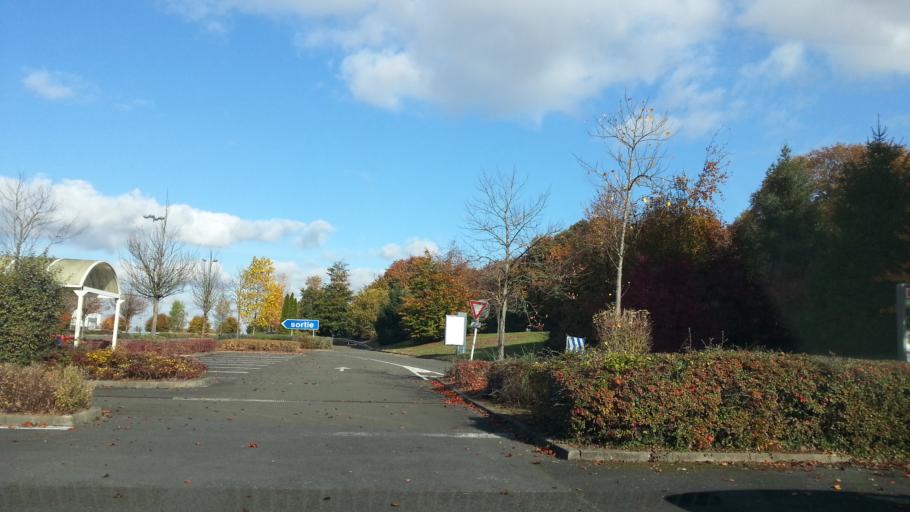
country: FR
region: Picardie
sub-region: Departement de l'Oise
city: Creil
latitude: 49.2372
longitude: 2.4719
